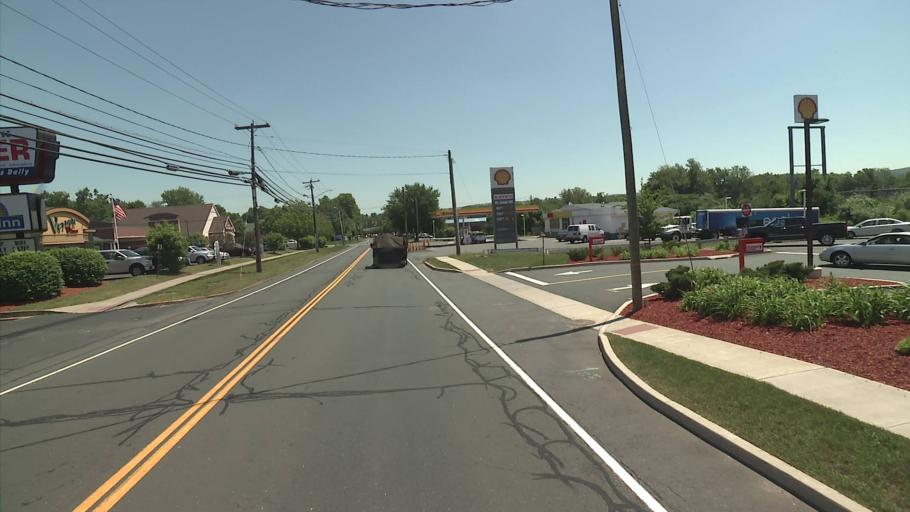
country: US
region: Connecticut
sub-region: Tolland County
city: Rockville
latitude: 41.8293
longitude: -72.4808
